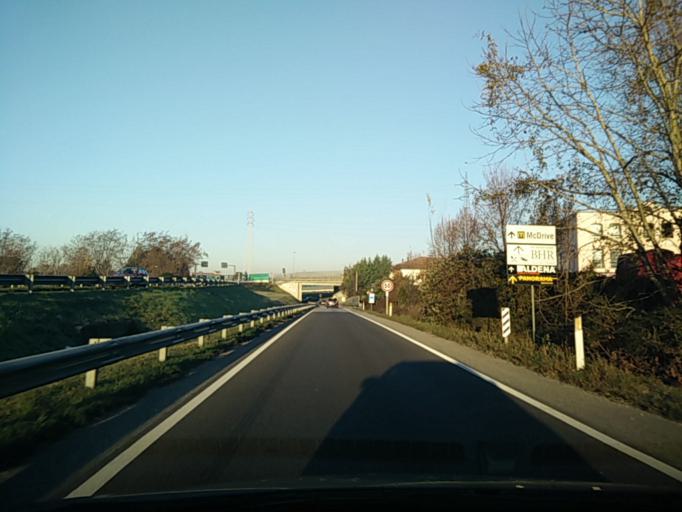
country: IT
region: Veneto
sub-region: Provincia di Treviso
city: Silea
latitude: 45.6554
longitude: 12.2859
